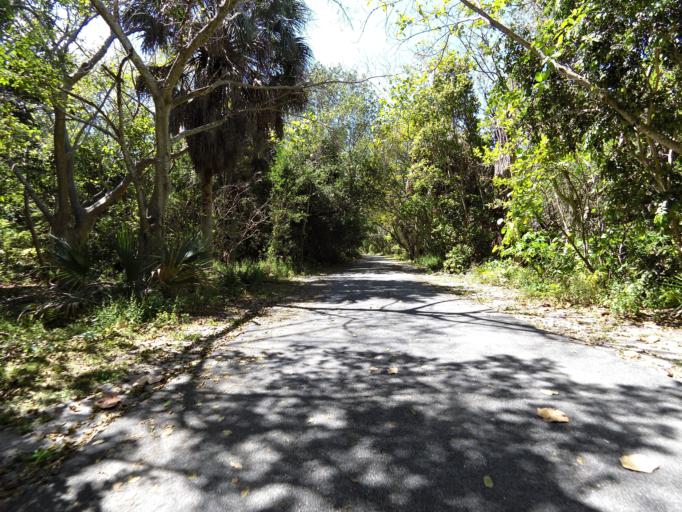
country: US
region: Florida
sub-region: Miami-Dade County
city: Key Biscayne
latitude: 25.6741
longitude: -80.1615
